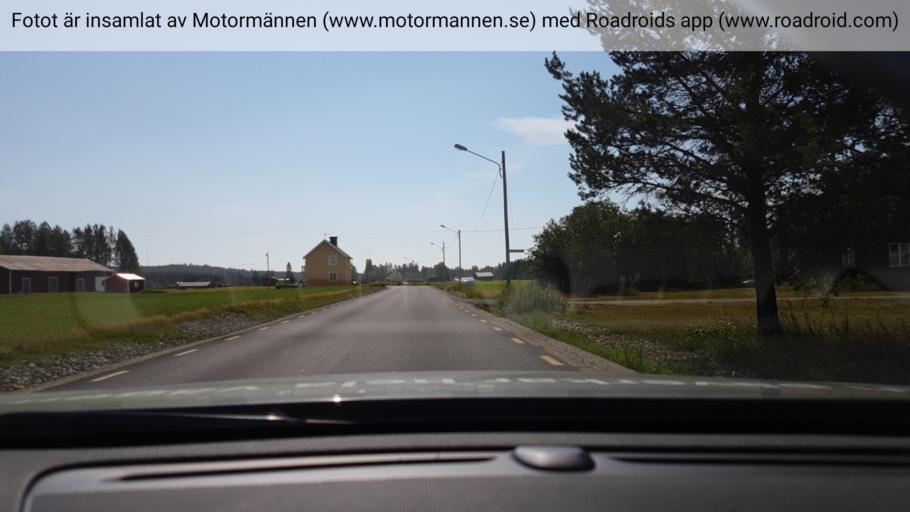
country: SE
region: Vaesterbotten
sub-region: Norsjo Kommun
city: Norsjoe
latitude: 64.5425
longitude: 19.3349
